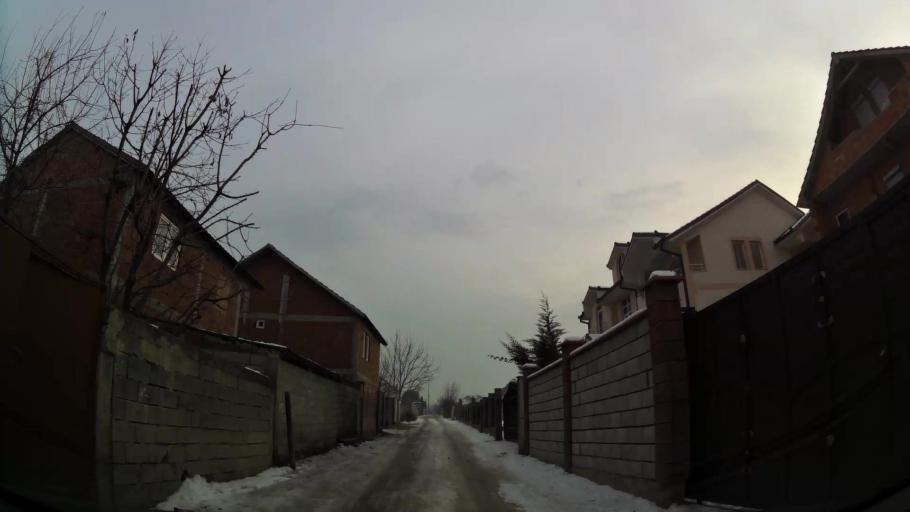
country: MK
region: Suto Orizari
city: Suto Orizare
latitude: 42.0383
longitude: 21.4150
